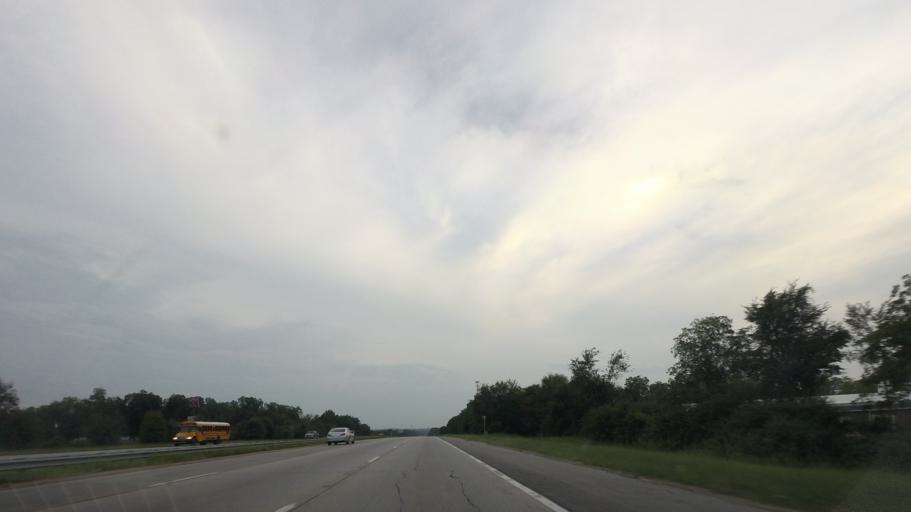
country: US
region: Georgia
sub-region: Bibb County
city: Macon
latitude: 32.7803
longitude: -83.6803
